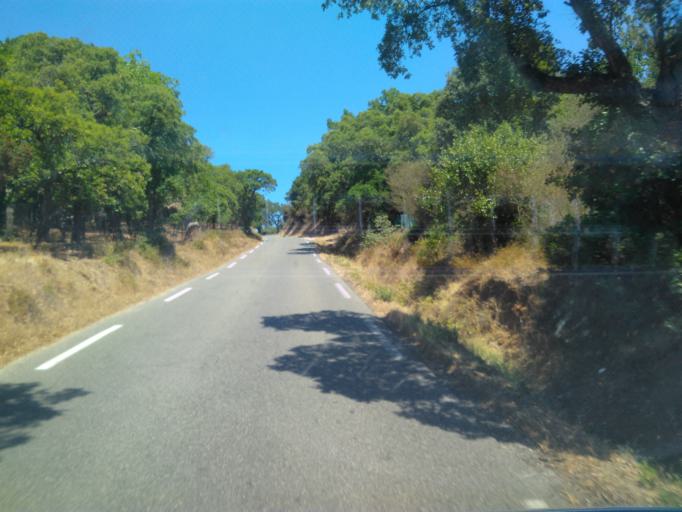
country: FR
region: Provence-Alpes-Cote d'Azur
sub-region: Departement du Var
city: Gassin
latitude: 43.2195
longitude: 6.5869
